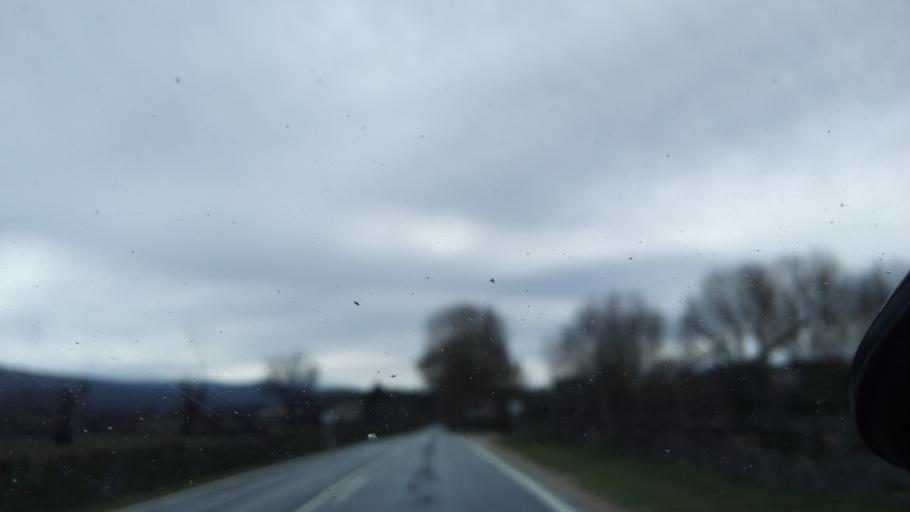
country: PT
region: Guarda
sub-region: Seia
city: Seia
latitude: 40.4929
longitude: -7.6574
